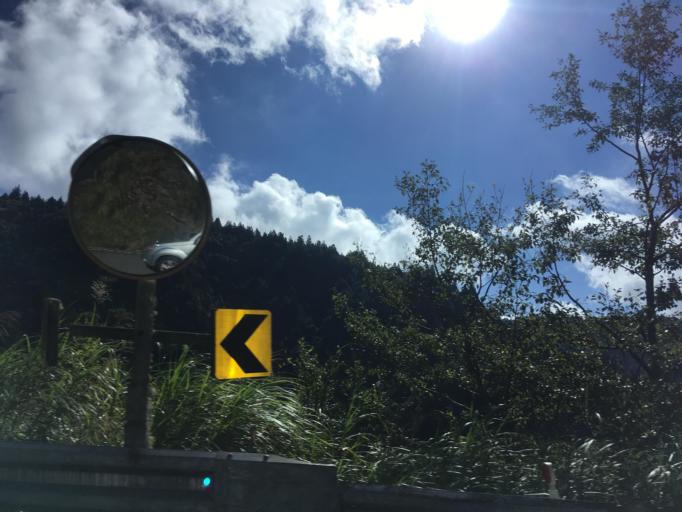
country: TW
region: Taiwan
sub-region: Yilan
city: Yilan
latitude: 24.5175
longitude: 121.5728
